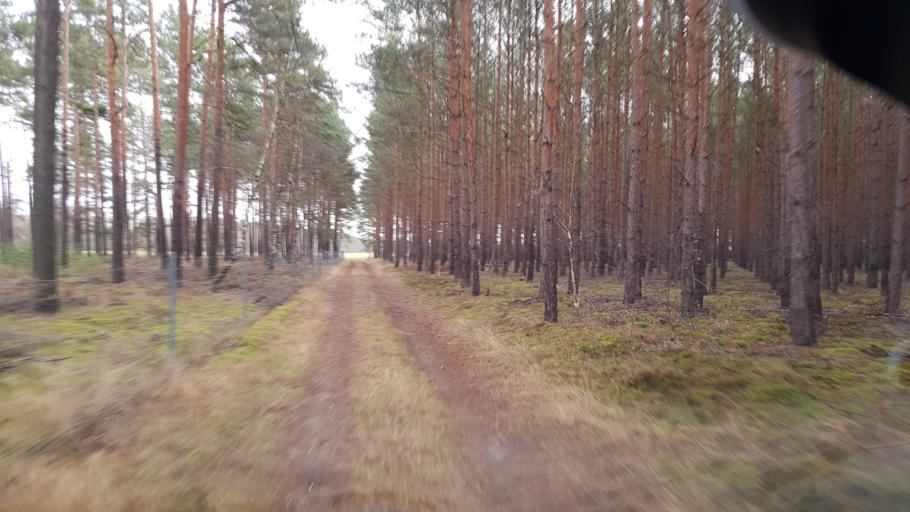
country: DE
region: Brandenburg
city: Altdobern
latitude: 51.6787
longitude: 14.0242
